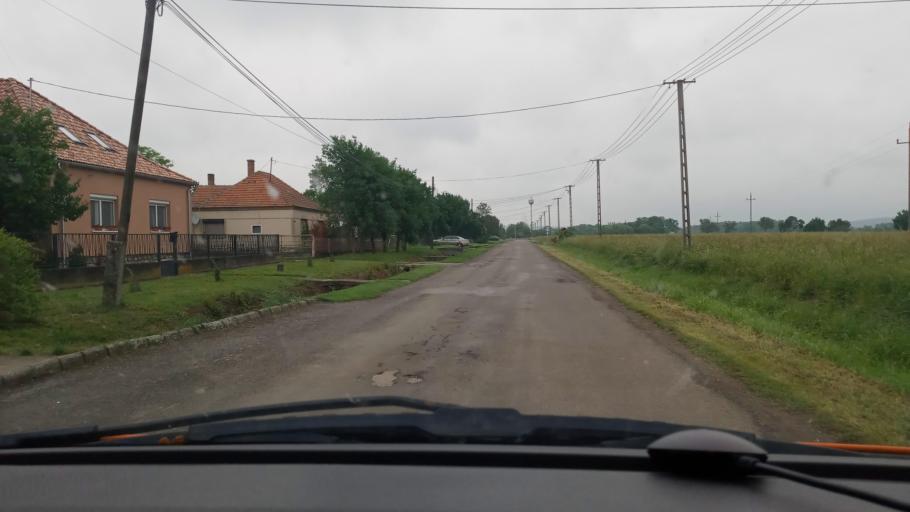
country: HU
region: Baranya
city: Szentlorinc
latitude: 46.0468
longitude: 17.9682
